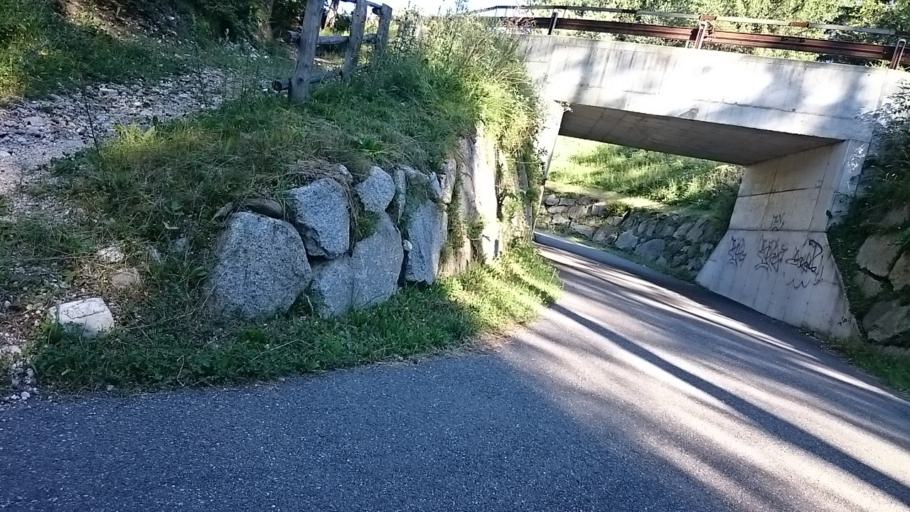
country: IT
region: Trentino-Alto Adige
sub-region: Bolzano
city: Braies
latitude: 46.7378
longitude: 12.1367
